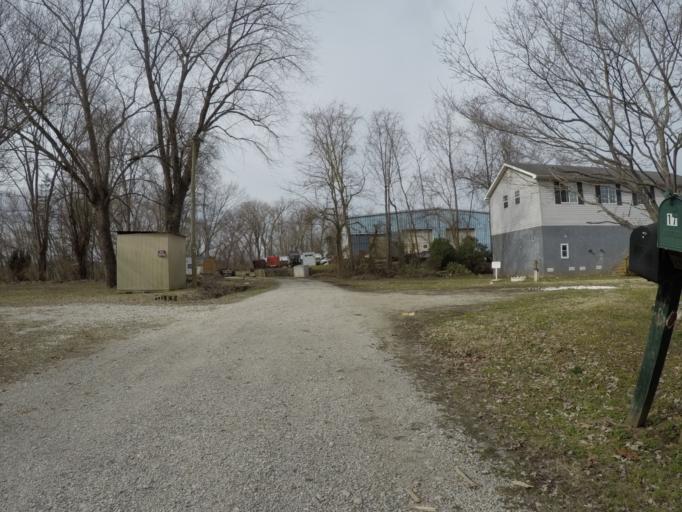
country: US
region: West Virginia
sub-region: Cabell County
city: Pea Ridge
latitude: 38.4392
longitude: -82.3663
